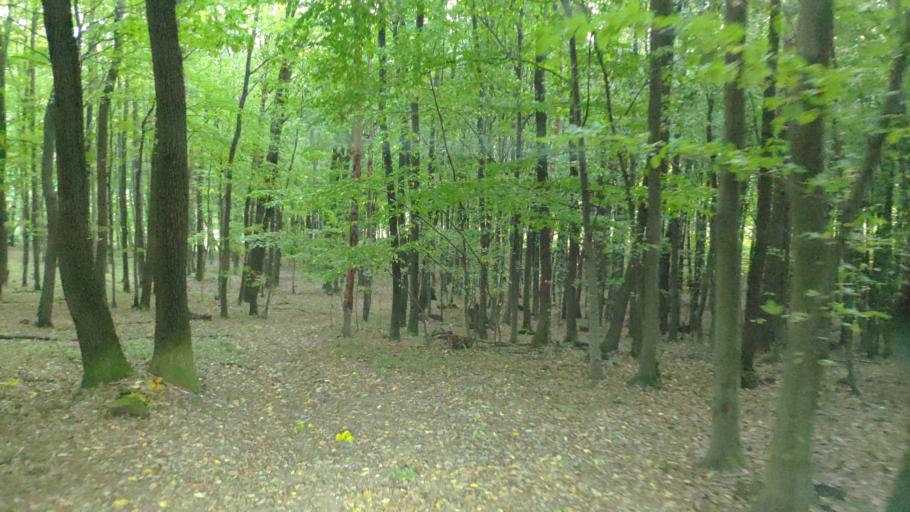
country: SK
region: Kosicky
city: Kosice
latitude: 48.7054
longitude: 21.1947
